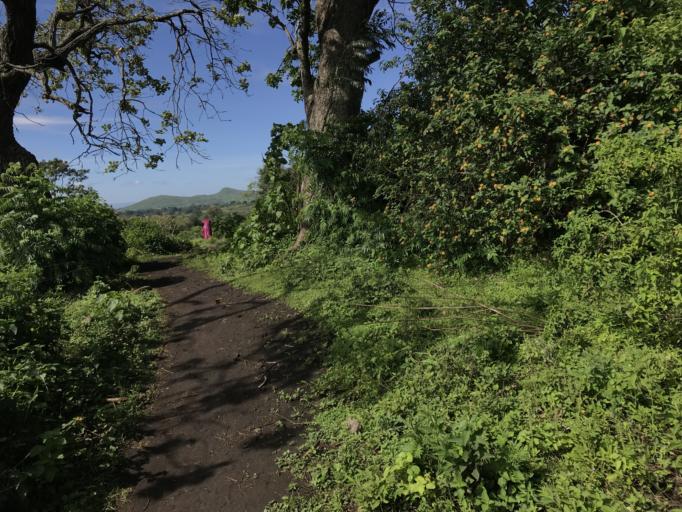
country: TZ
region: Arusha
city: Usa River
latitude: -3.3941
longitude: 36.7972
